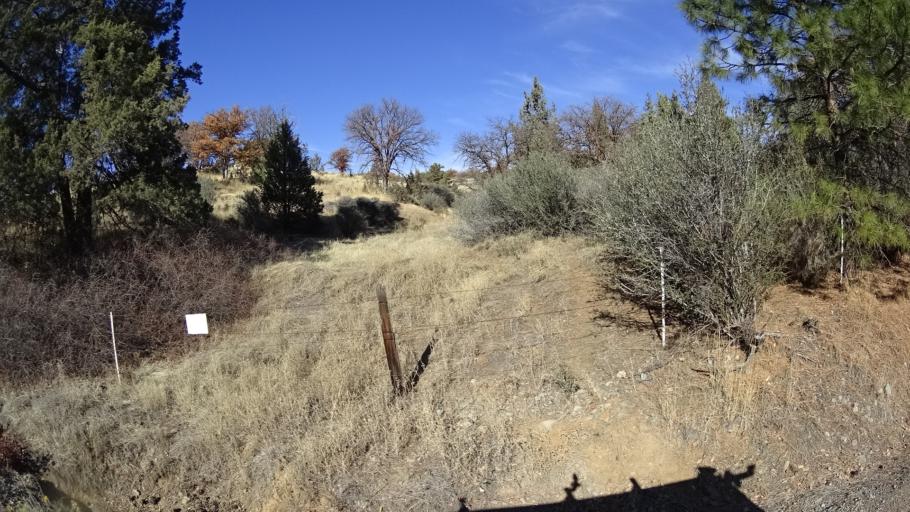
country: US
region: California
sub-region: Siskiyou County
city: Yreka
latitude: 41.7606
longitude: -122.6334
